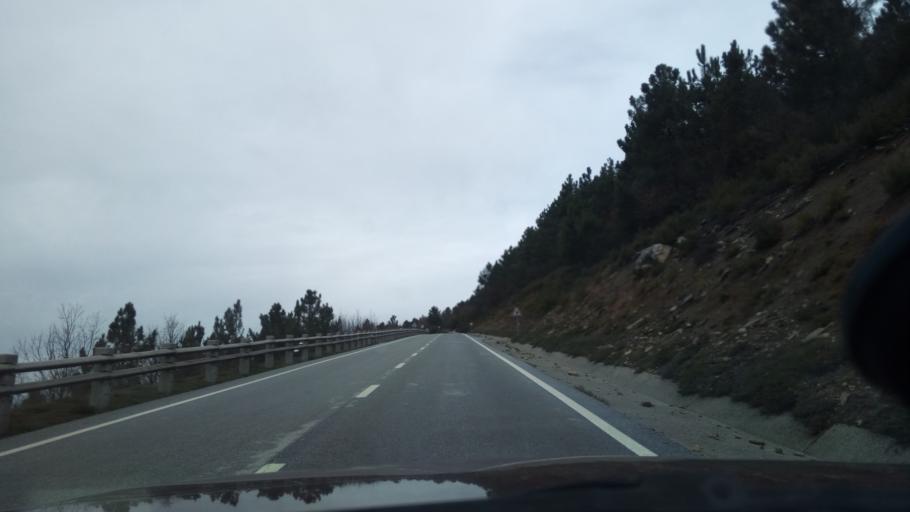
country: PT
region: Guarda
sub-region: Seia
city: Seia
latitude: 40.3436
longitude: -7.7127
